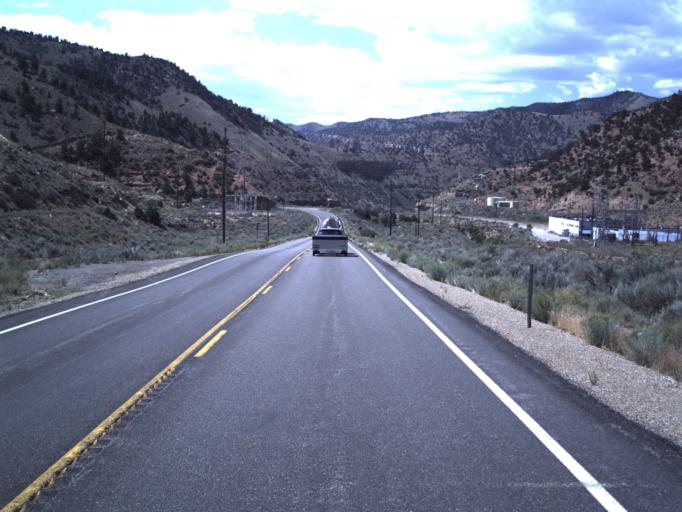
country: US
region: Utah
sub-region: Carbon County
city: Helper
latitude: 39.7364
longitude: -110.8466
